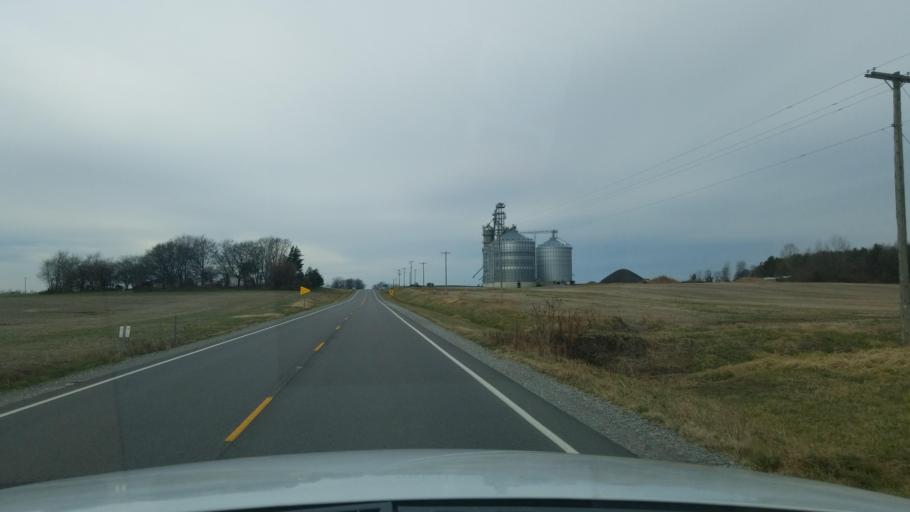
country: US
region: Illinois
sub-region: White County
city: Carmi
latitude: 37.9077
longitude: -88.1495
